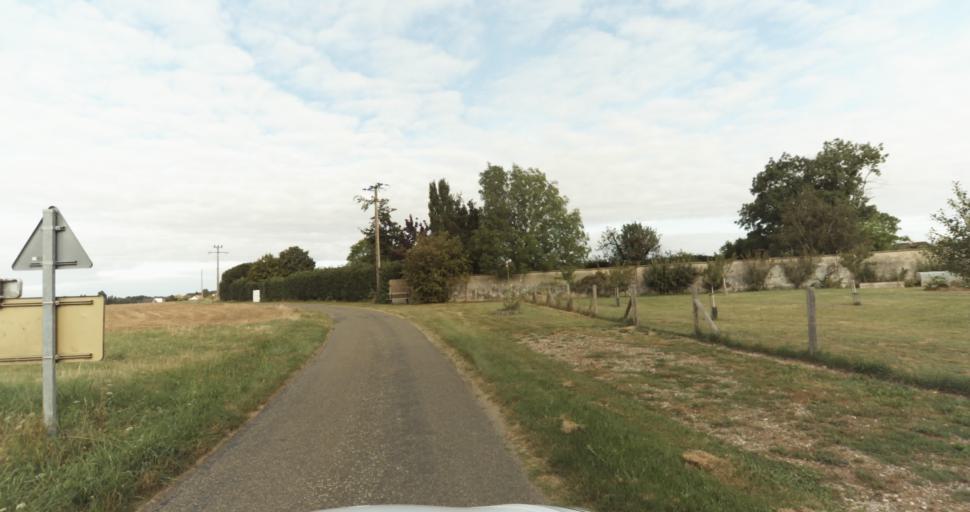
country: FR
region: Haute-Normandie
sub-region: Departement de l'Eure
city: Saint-Germain-sur-Avre
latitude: 48.8187
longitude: 1.2794
